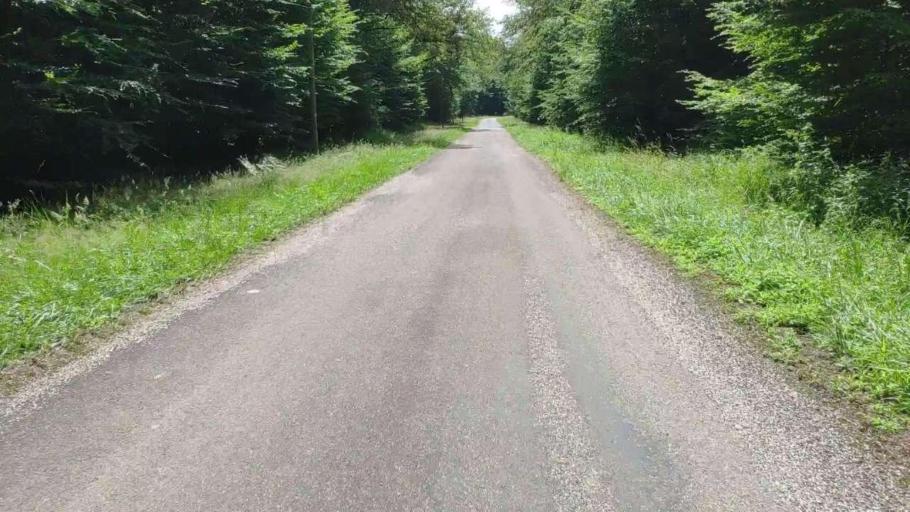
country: FR
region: Franche-Comte
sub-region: Departement du Jura
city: Chaussin
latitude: 46.8834
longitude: 5.4641
